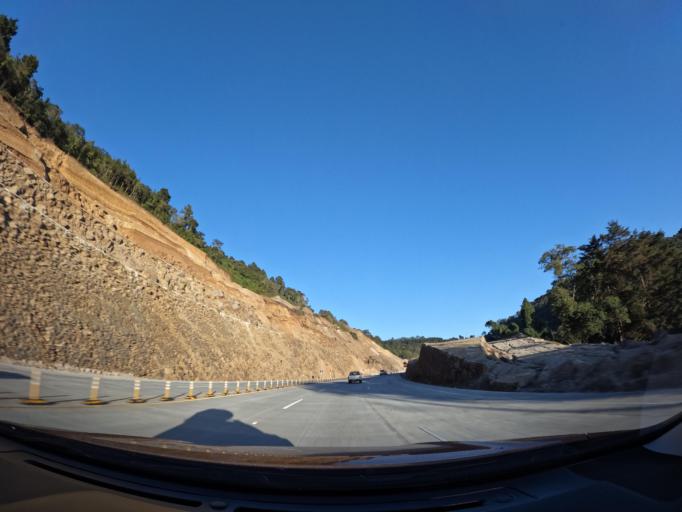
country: GT
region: Guatemala
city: Villa Canales
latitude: 14.4867
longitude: -90.4956
